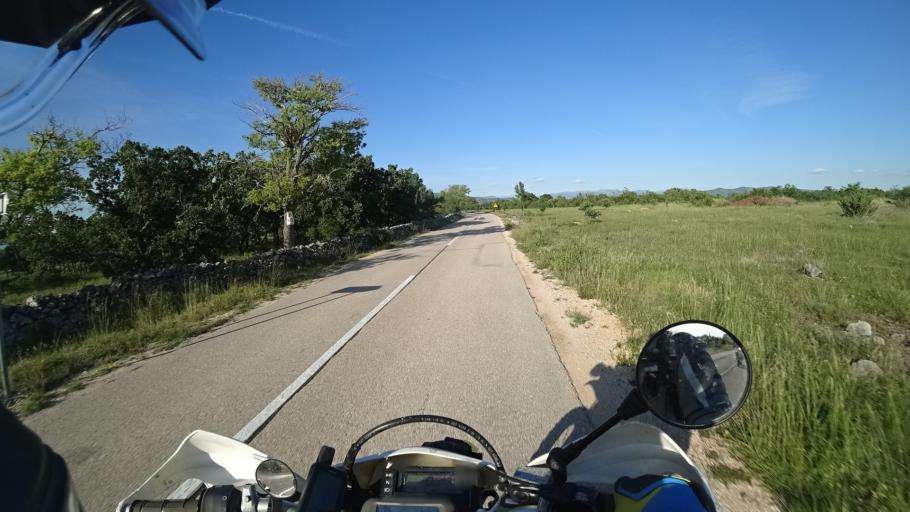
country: HR
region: Sibensko-Kniniska
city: Drnis
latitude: 43.8528
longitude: 16.0669
